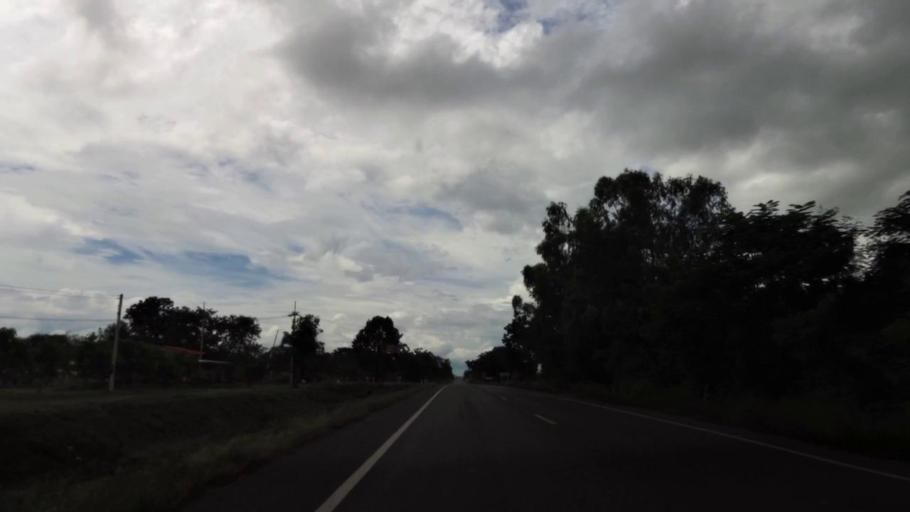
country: TH
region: Nakhon Sawan
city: Phai Sali
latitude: 15.5993
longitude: 100.6768
